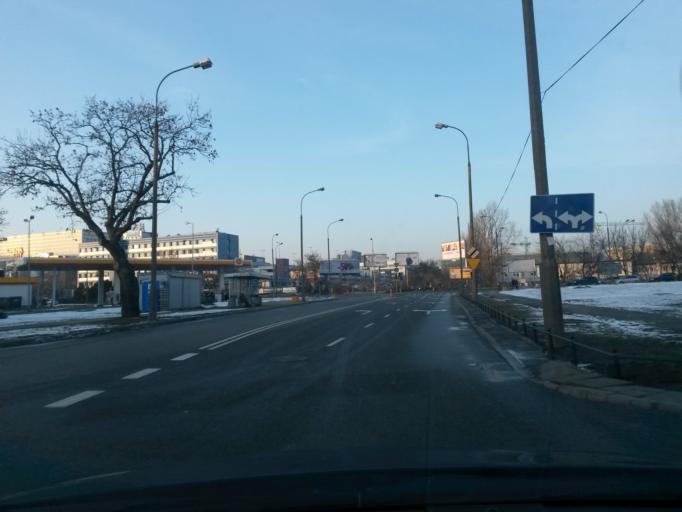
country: PL
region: Masovian Voivodeship
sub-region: Warszawa
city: Mokotow
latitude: 52.1771
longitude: 21.0075
